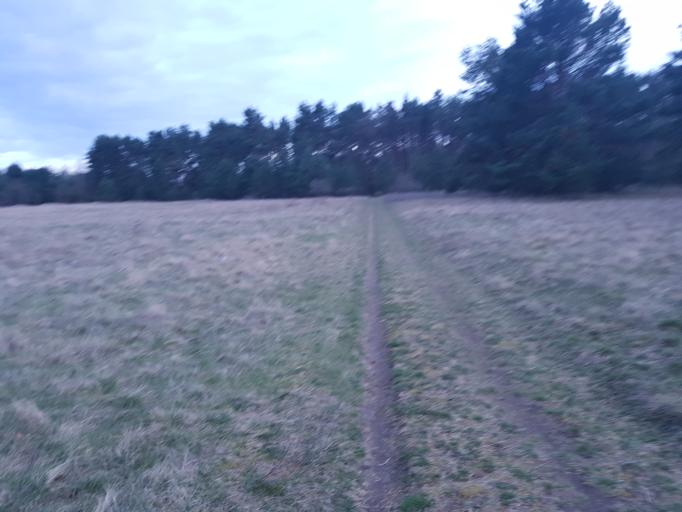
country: DE
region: Brandenburg
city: Eisenhuettenstadt
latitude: 52.1564
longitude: 14.6670
